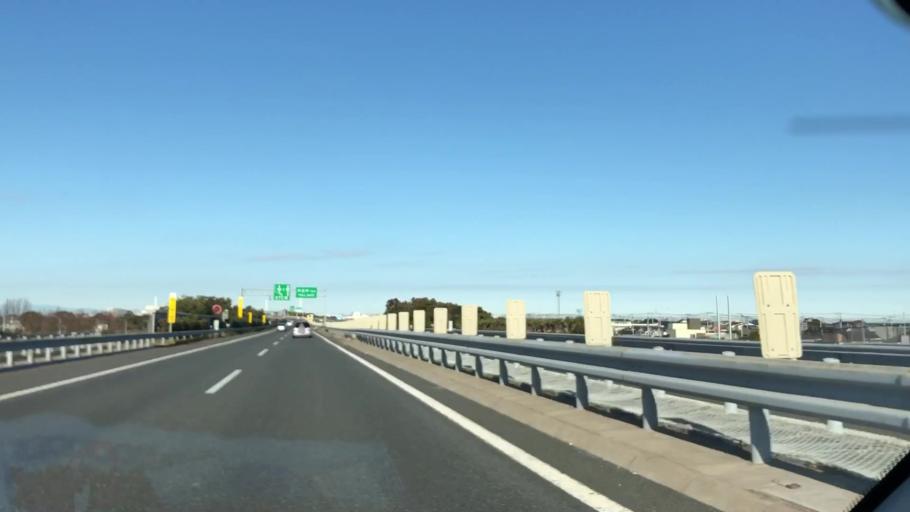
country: JP
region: Chiba
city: Kisarazu
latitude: 35.4288
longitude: 139.9276
